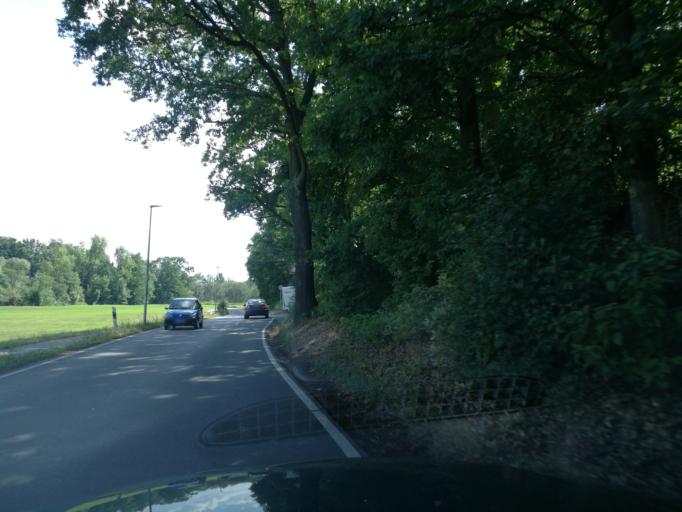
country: DE
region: Bavaria
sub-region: Regierungsbezirk Mittelfranken
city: Furth
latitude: 49.4976
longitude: 10.9690
